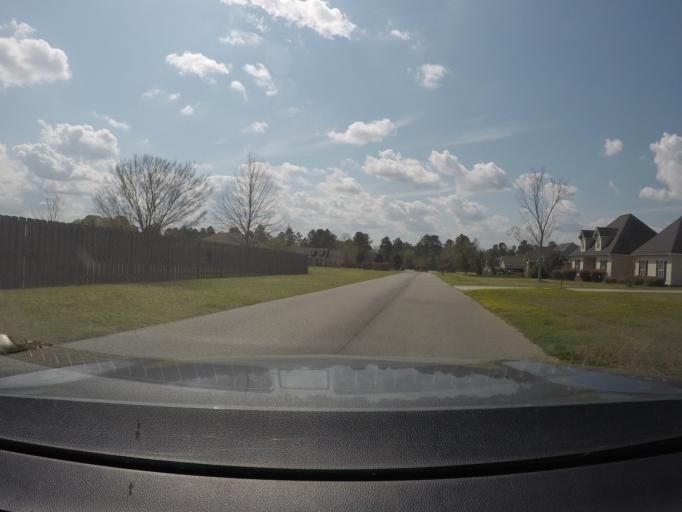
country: US
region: Georgia
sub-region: Bulloch County
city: Statesboro
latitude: 32.3583
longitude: -81.7582
